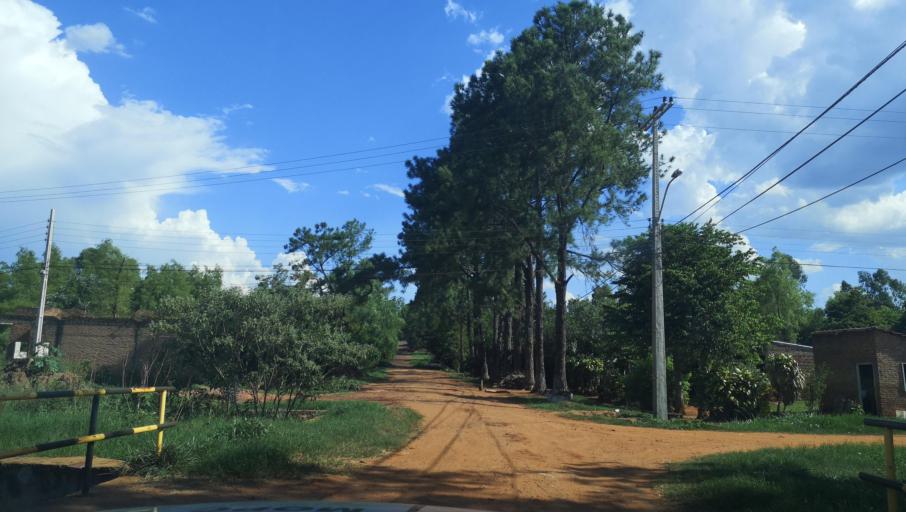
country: PY
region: Misiones
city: Santa Maria
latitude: -26.8823
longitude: -57.0190
